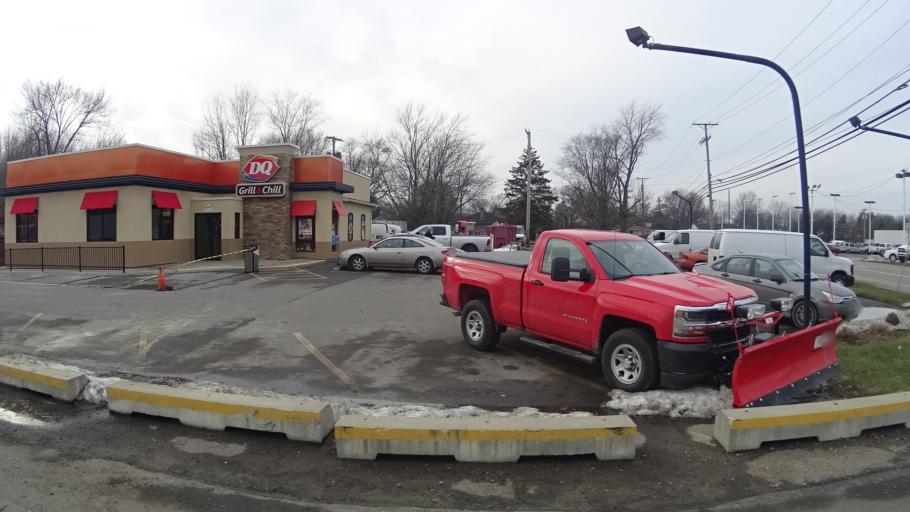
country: US
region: Ohio
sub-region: Lorain County
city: Amherst
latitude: 41.3887
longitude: -82.2101
